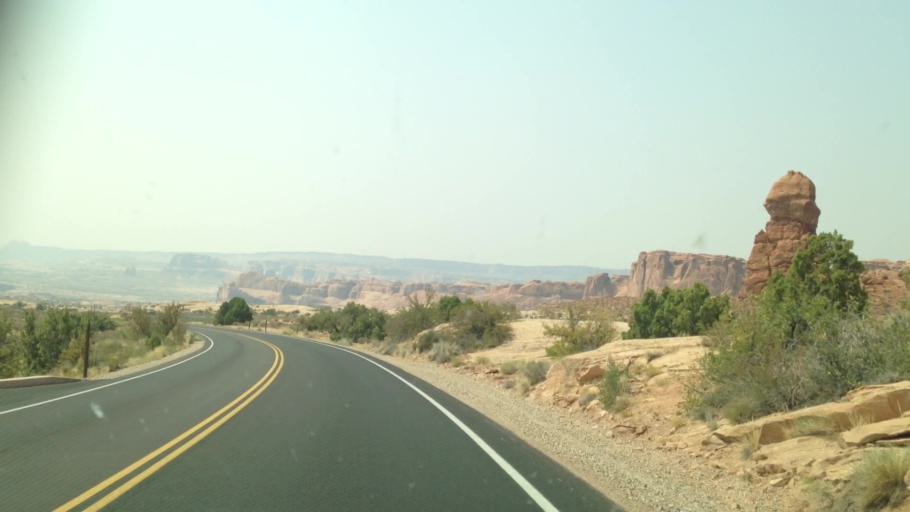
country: US
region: Utah
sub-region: Grand County
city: Moab
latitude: 38.6855
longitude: -109.5820
